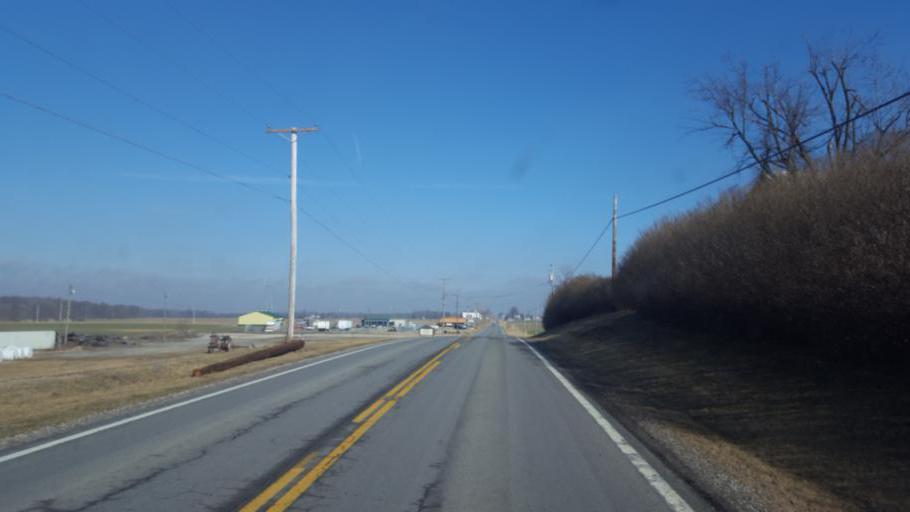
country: US
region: Ohio
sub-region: Crawford County
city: Bucyrus
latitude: 40.8415
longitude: -82.9697
